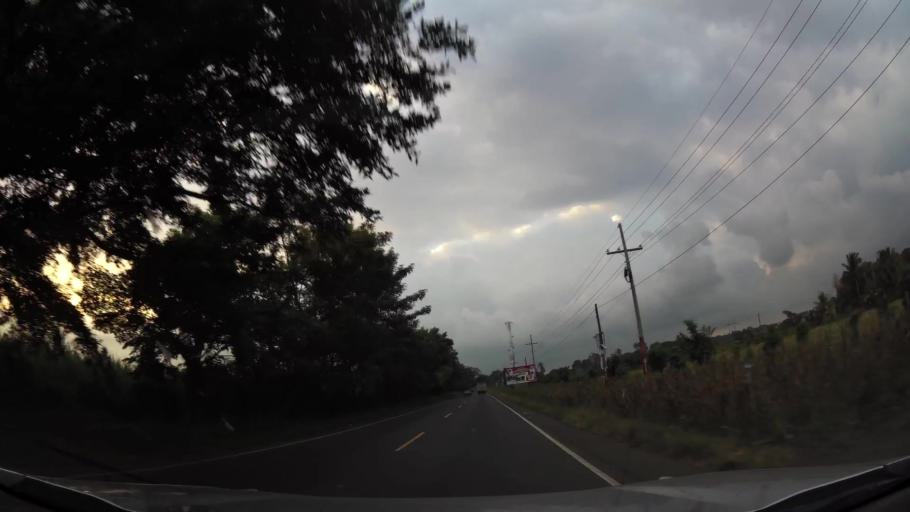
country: GT
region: Escuintla
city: Siquinala
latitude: 14.3001
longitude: -90.9535
